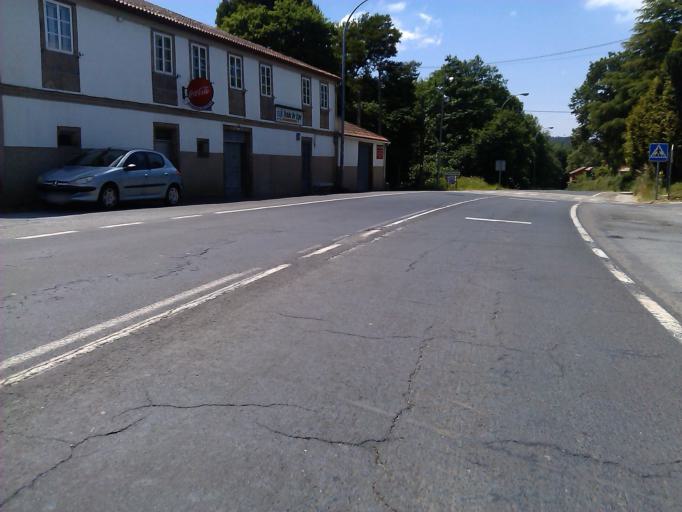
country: ES
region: Galicia
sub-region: Provincia da Coruna
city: Oroso
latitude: 42.8992
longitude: -8.4441
